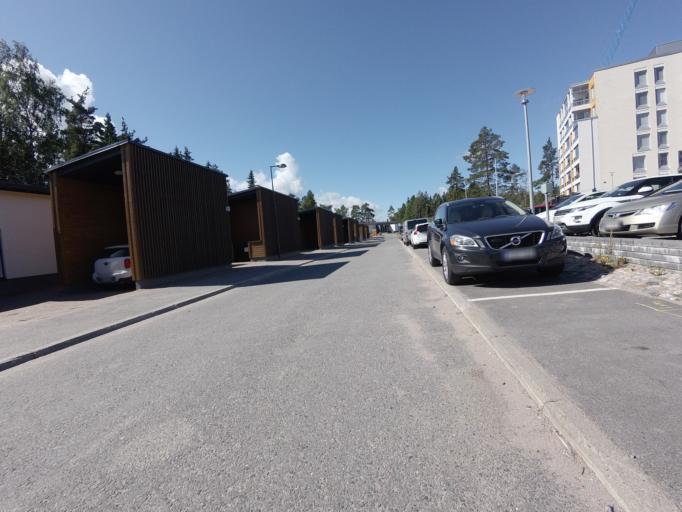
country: FI
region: Uusimaa
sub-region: Helsinki
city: Espoo
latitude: 60.1510
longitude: 24.6034
